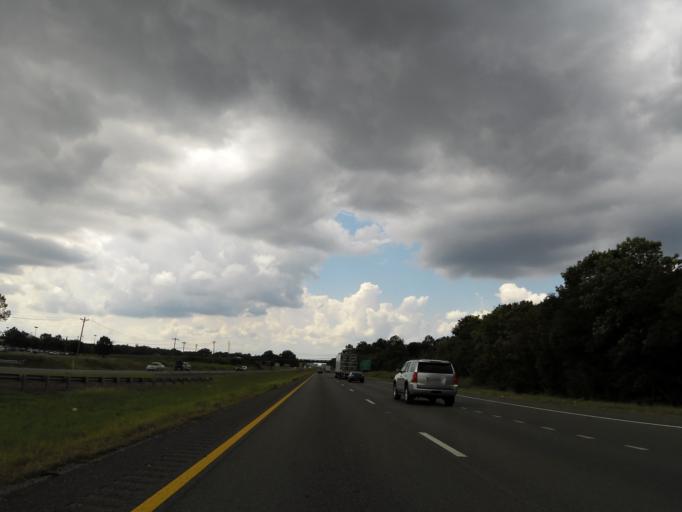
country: US
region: Tennessee
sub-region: Wilson County
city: Lebanon
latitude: 36.1824
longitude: -86.3024
